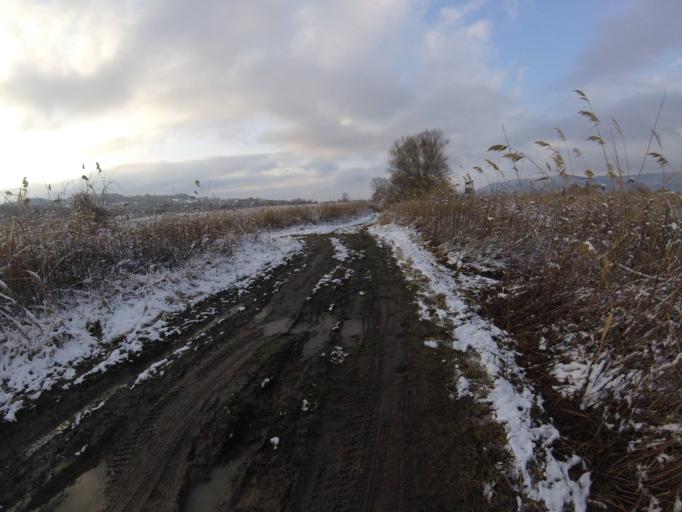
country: HU
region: Komarom-Esztergom
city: Esztergom
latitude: 47.8006
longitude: 18.7889
